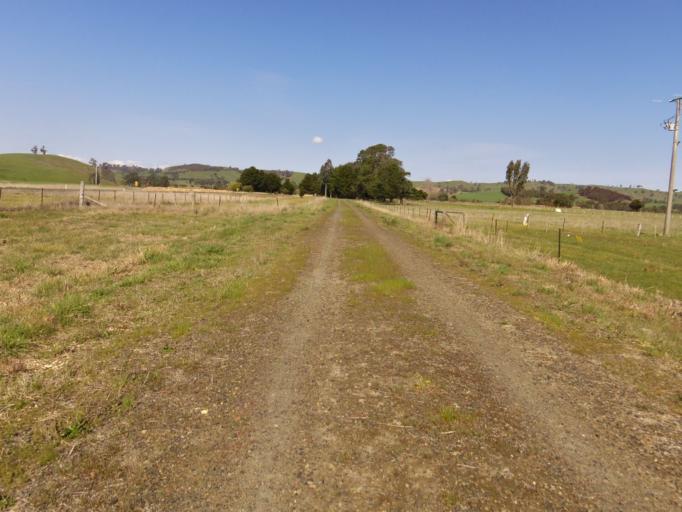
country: AU
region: Victoria
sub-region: Murrindindi
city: Alexandra
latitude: -37.0064
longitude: 145.7504
